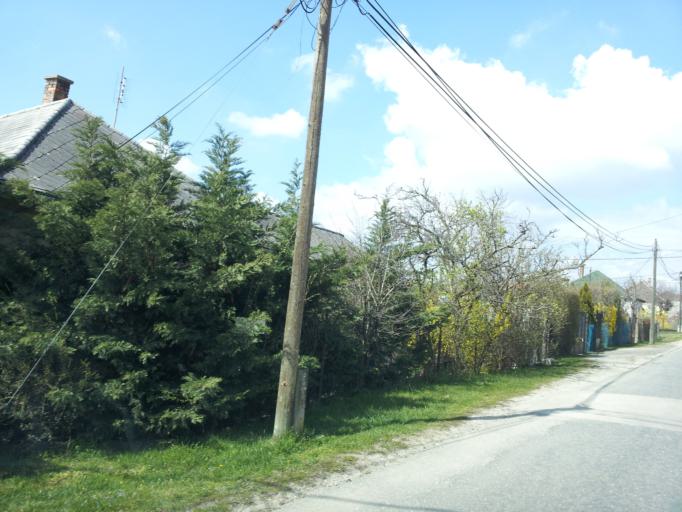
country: HU
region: Pest
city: Erd
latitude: 47.3999
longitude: 18.9126
